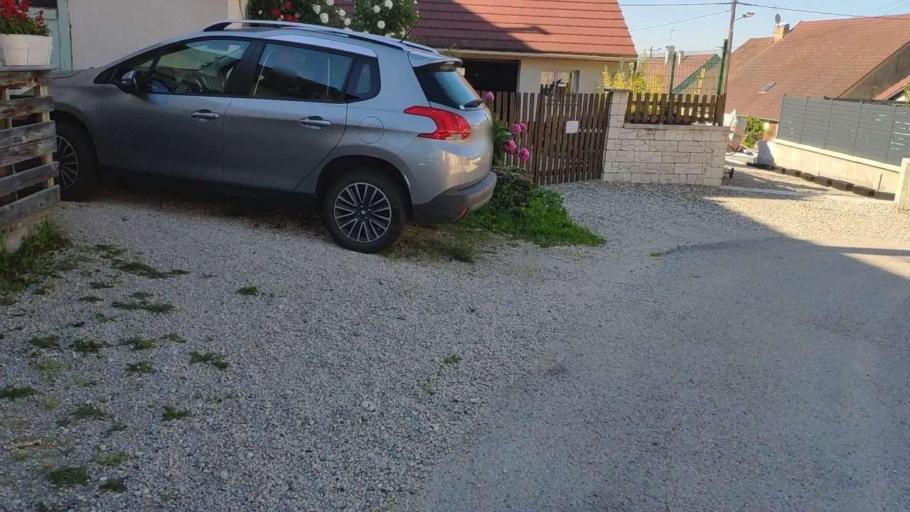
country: FR
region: Franche-Comte
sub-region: Departement du Jura
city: Montmorot
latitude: 46.7329
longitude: 5.5553
